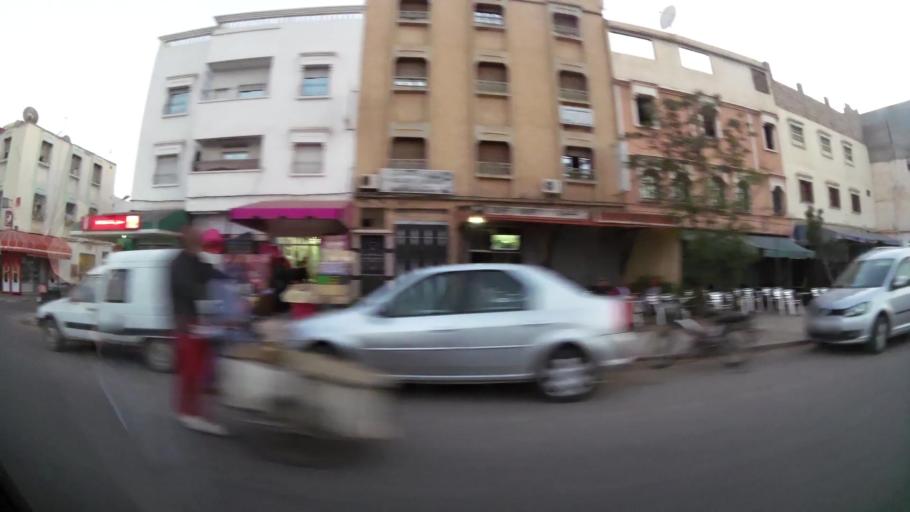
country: MA
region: Souss-Massa-Draa
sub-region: Inezgane-Ait Mellou
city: Inezgane
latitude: 30.3767
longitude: -9.4967
